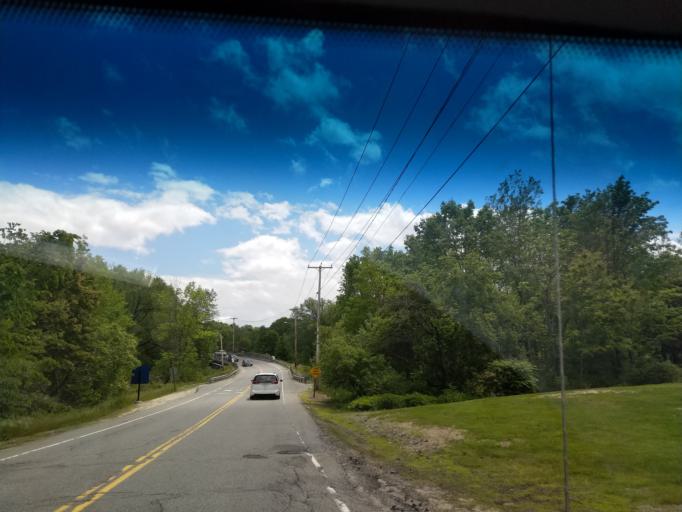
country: US
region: Maine
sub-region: Cumberland County
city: Falmouth
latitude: 43.7396
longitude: -70.2881
